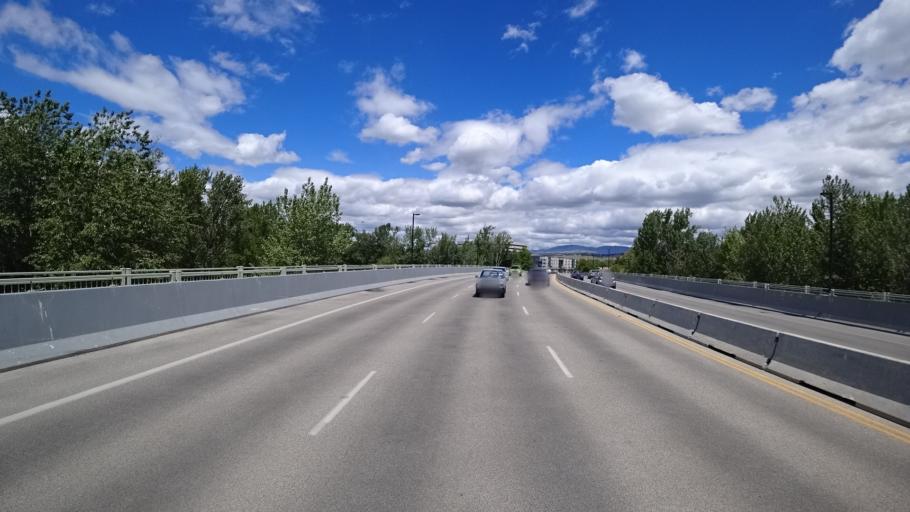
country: US
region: Idaho
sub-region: Ada County
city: Boise
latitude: 43.6004
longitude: -116.1886
